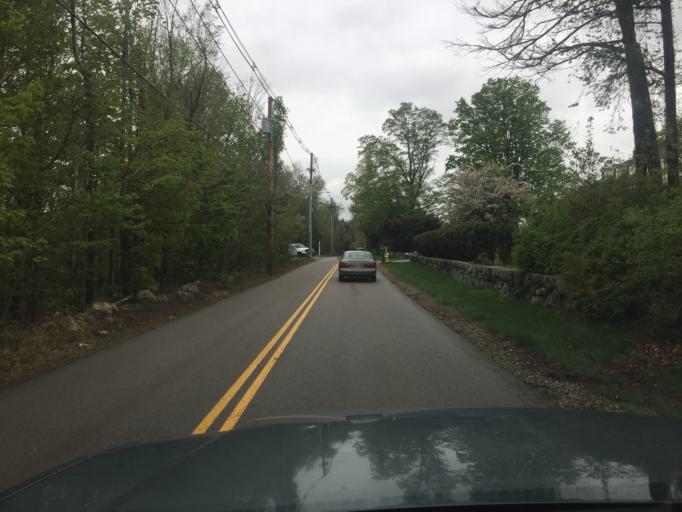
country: US
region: Massachusetts
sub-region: Norfolk County
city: Westwood
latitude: 42.2257
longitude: -71.2143
